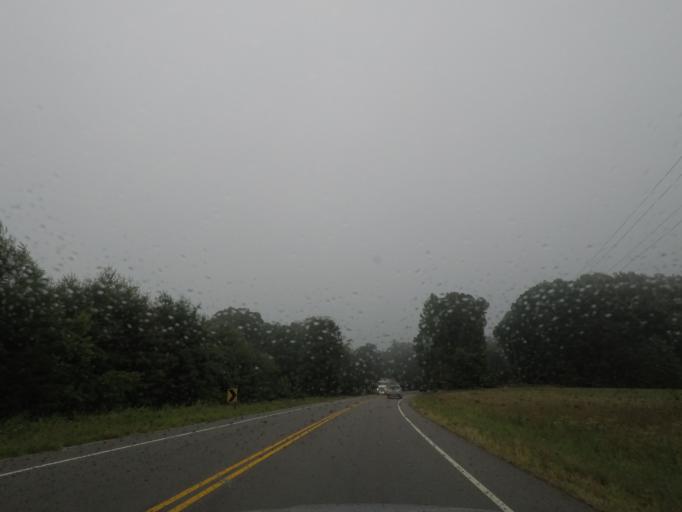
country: US
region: Virginia
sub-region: Prince Edward County
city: Farmville
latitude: 37.3926
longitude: -78.4849
